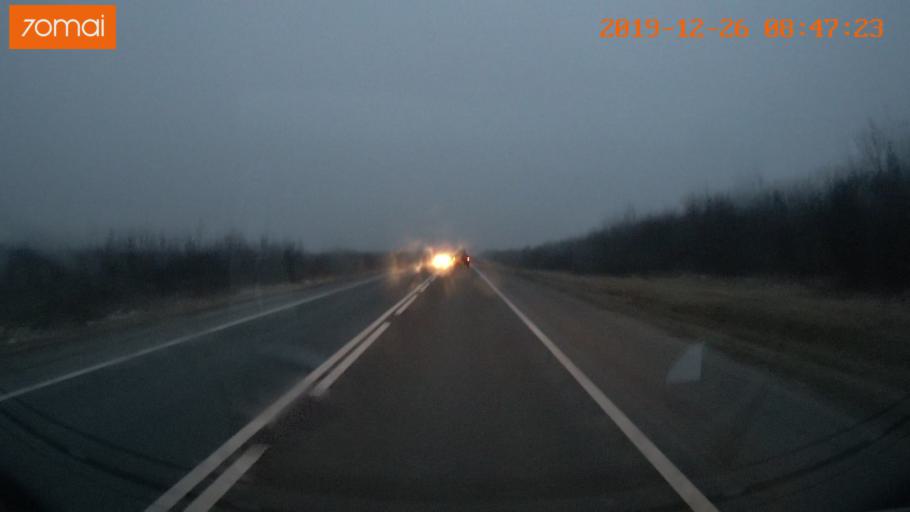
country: RU
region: Jaroslavl
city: Prechistoye
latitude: 58.6223
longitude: 40.3318
